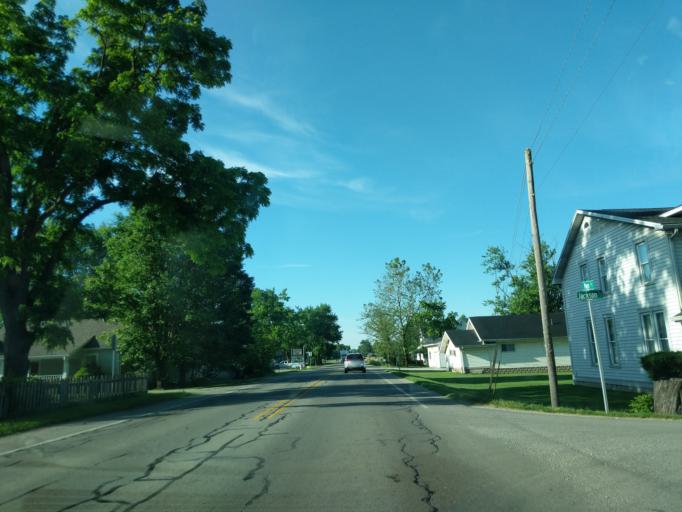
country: US
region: Indiana
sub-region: Hancock County
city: Greenfield
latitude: 39.8567
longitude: -85.7700
